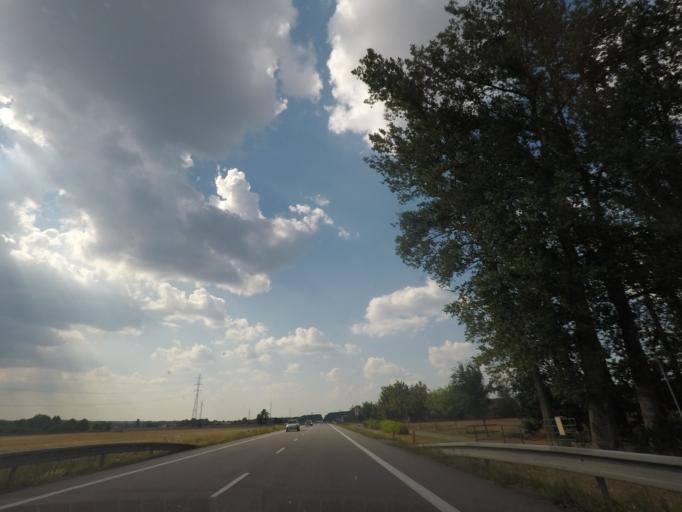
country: CZ
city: Albrechtice nad Orlici
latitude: 50.1658
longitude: 16.0487
